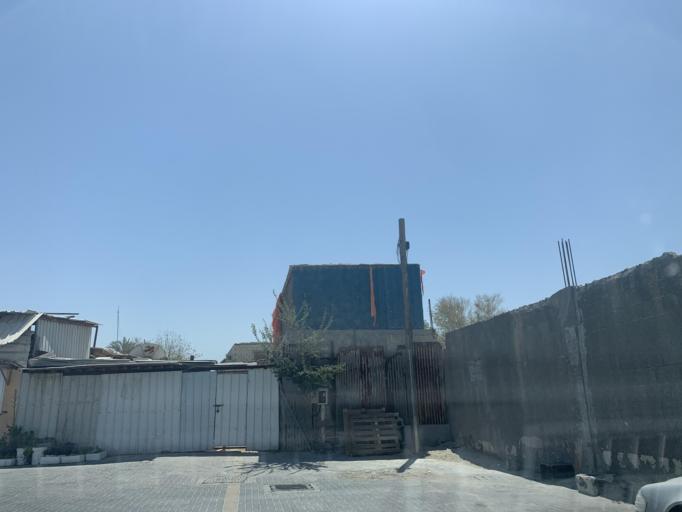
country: BH
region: Muharraq
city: Al Muharraq
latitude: 26.2528
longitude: 50.6288
